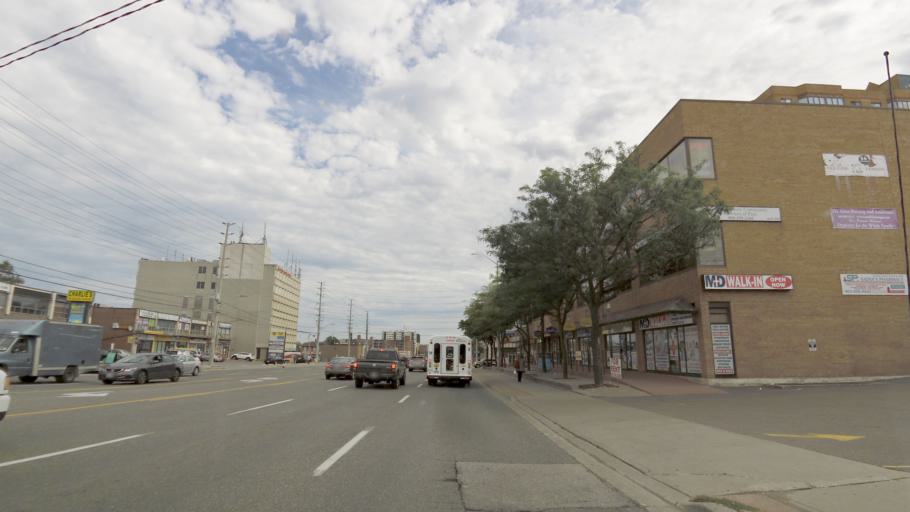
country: CA
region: Ontario
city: Mississauga
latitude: 43.5815
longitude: -79.6183
